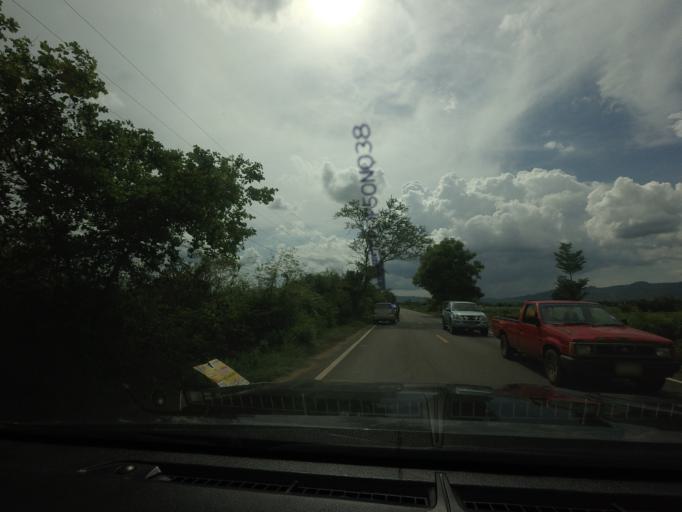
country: TH
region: Kanchanaburi
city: Bo Phloi
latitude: 14.1670
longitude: 99.4443
